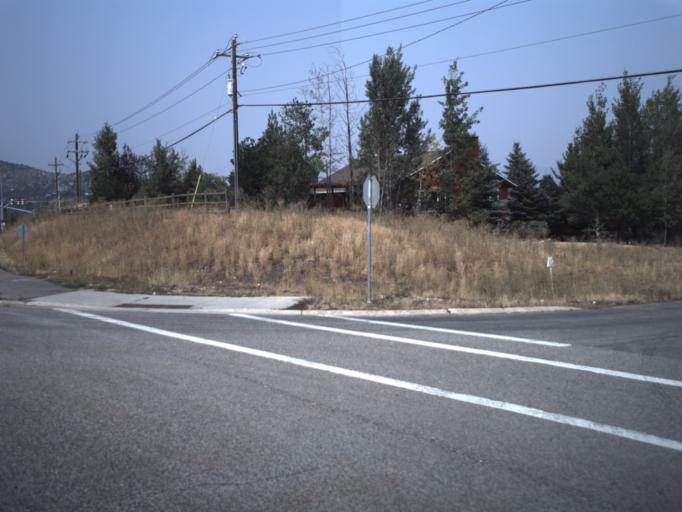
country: US
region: Utah
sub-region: Summit County
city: Snyderville
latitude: 40.6863
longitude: -111.5431
